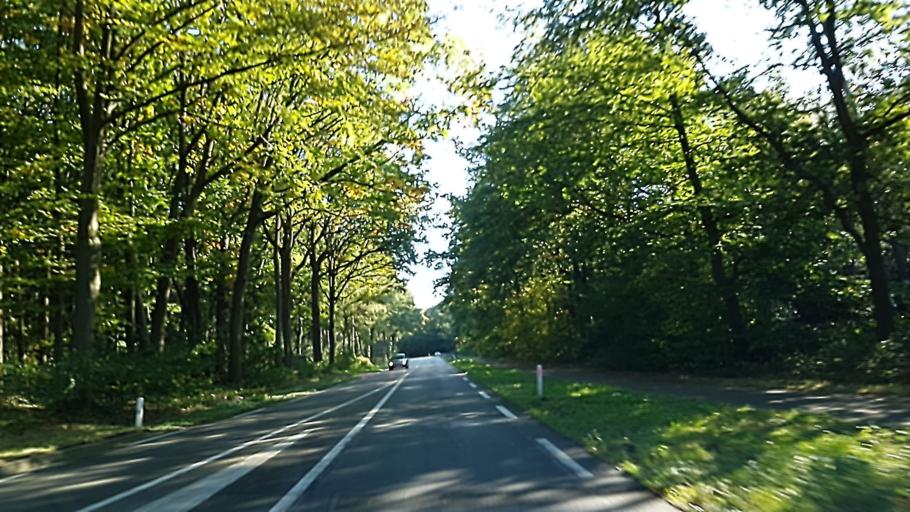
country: BE
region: Flanders
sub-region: Provincie Antwerpen
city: Stabroek
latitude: 51.3927
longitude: 4.3587
